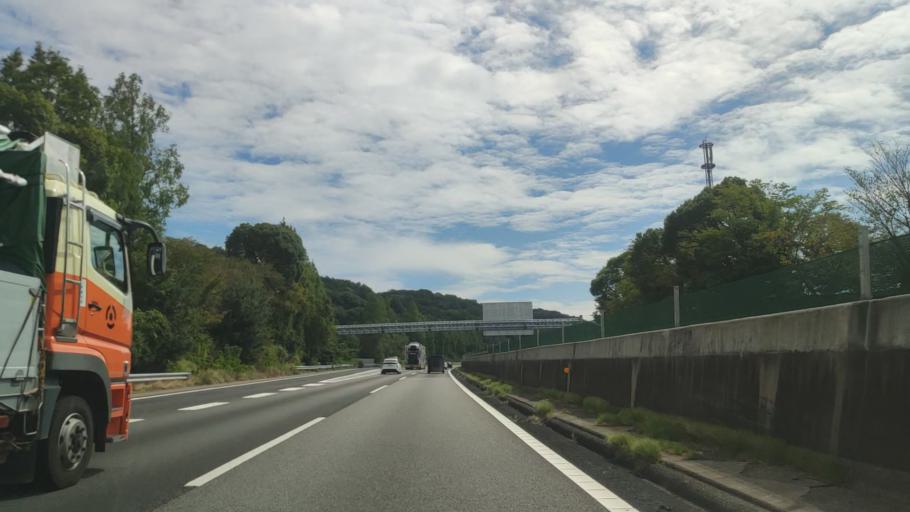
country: JP
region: Aichi
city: Okazaki
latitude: 35.0119
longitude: 137.1711
